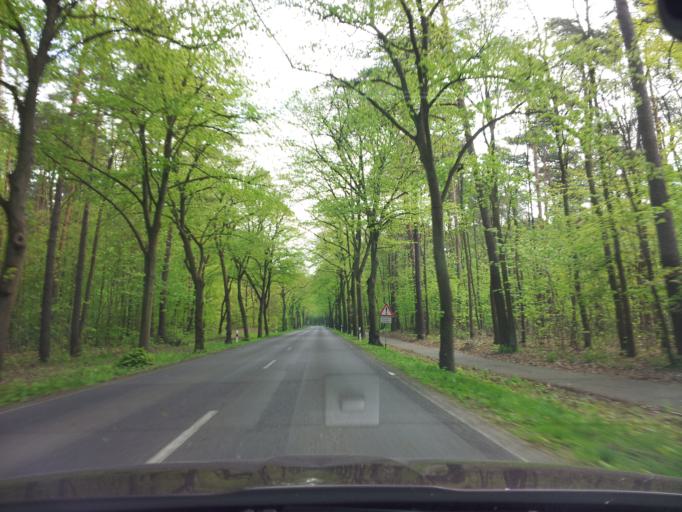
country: DE
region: Brandenburg
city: Grunheide
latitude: 52.4361
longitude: 13.8384
